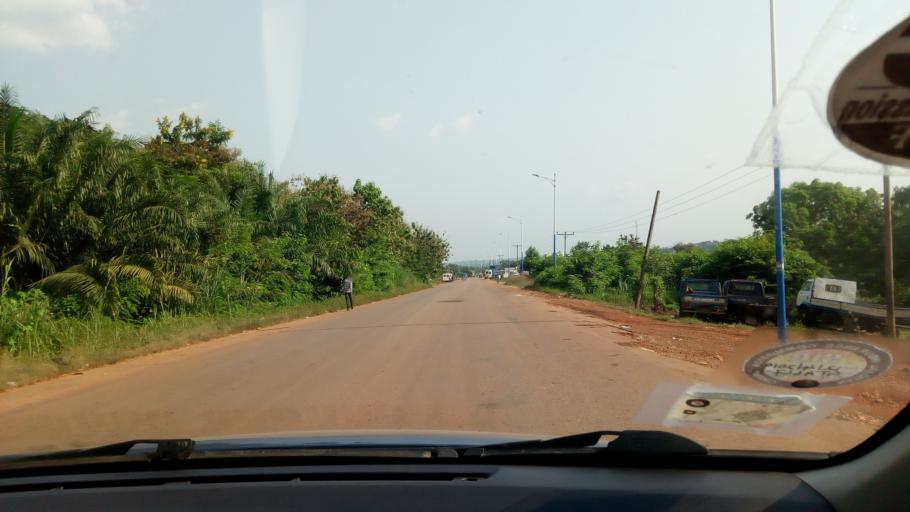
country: GH
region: Western
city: Bibiani
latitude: 6.8037
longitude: -2.5238
